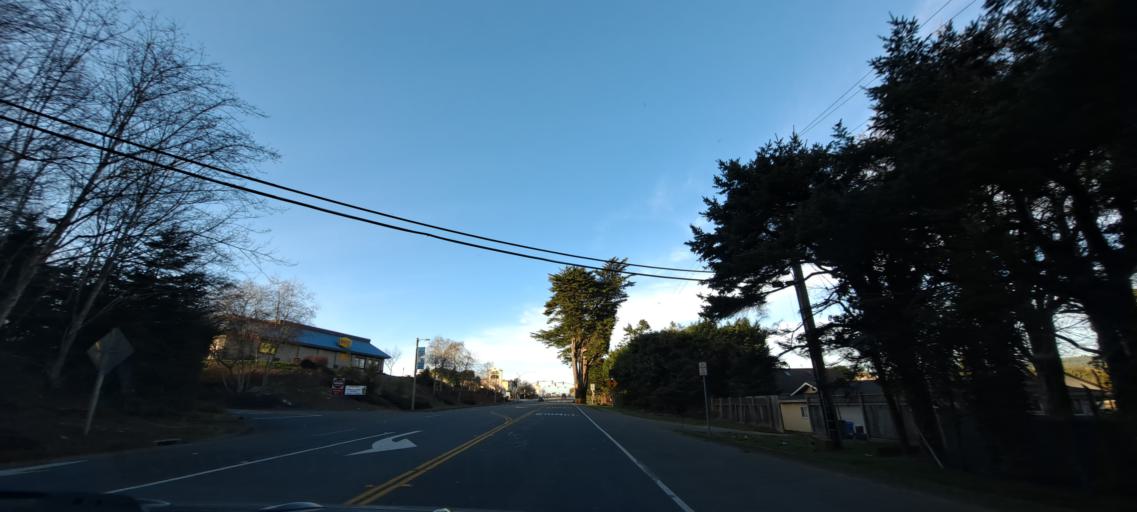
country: US
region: California
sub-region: Humboldt County
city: McKinleyville
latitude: 40.9310
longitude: -124.1008
